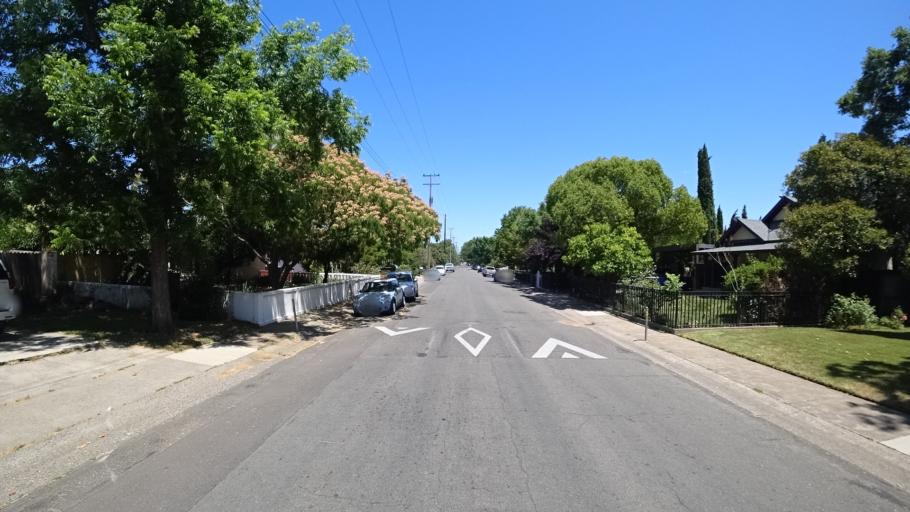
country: US
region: California
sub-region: Sacramento County
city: Florin
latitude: 38.5403
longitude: -121.4329
